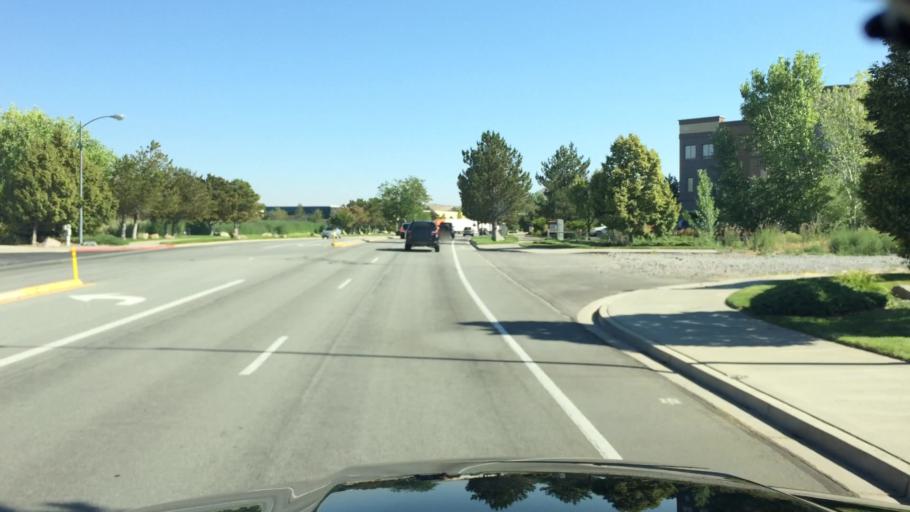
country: US
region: Nevada
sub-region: Washoe County
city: Sparks
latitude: 39.4432
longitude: -119.7605
